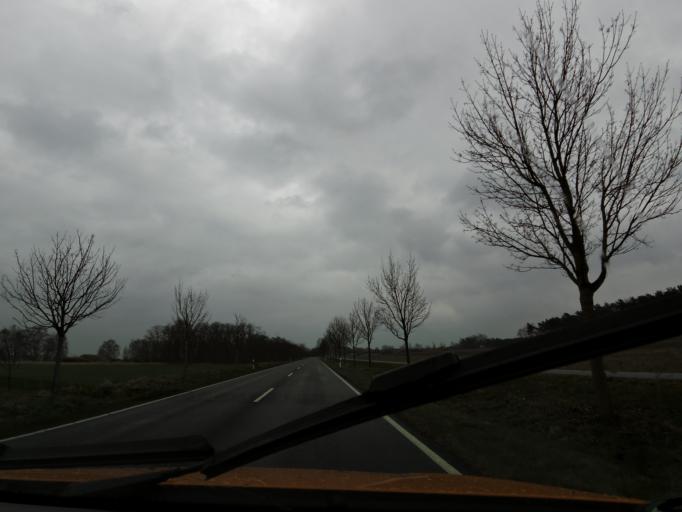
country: DE
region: Brandenburg
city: Ziesar
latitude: 52.2716
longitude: 12.2666
